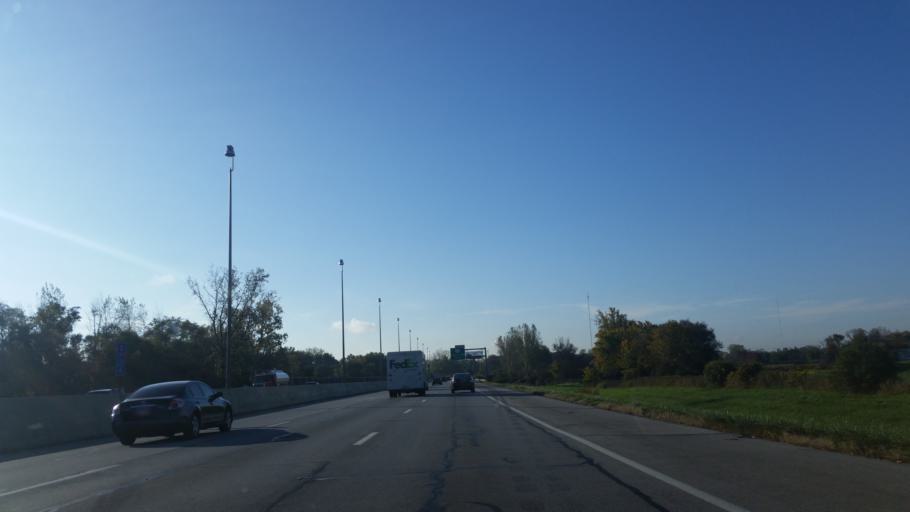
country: US
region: Ohio
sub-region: Summit County
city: Fairlawn
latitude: 41.0939
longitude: -81.5854
